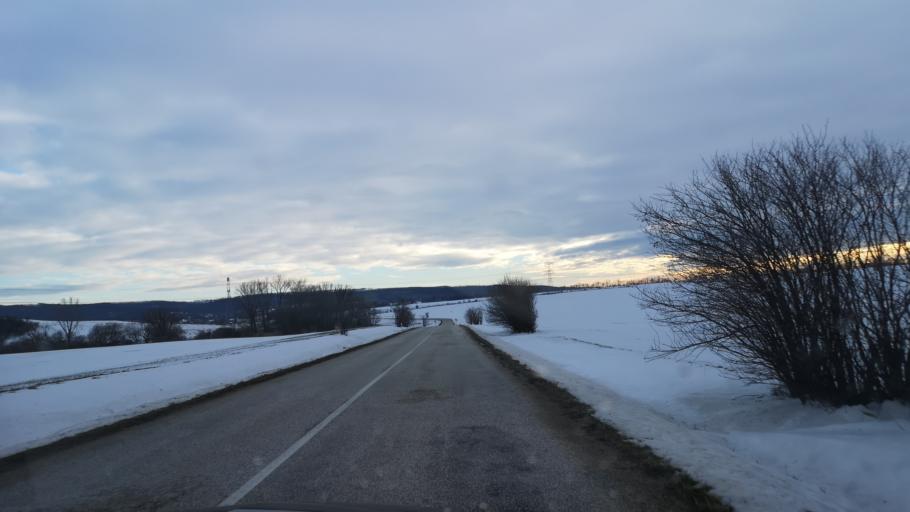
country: SK
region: Nitriansky
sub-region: Okres Nitra
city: Vrable
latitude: 48.1252
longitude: 18.3342
